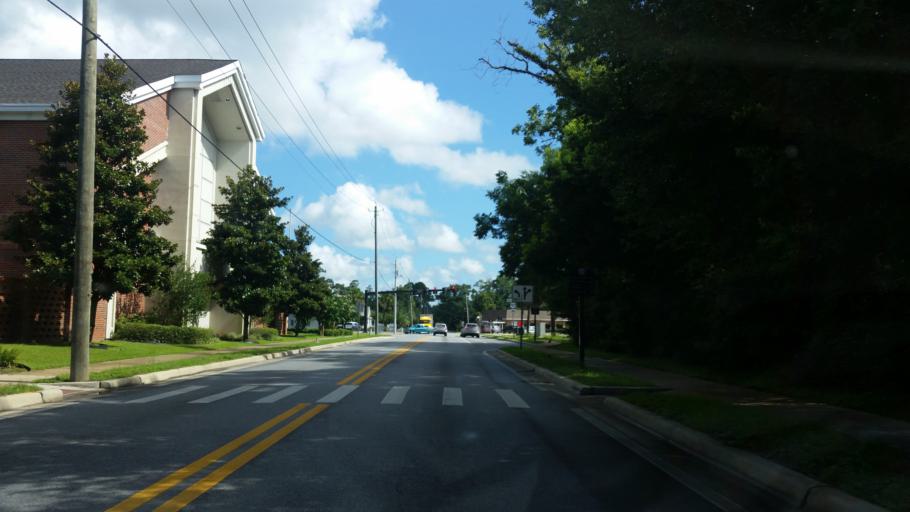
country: US
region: Florida
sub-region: Santa Rosa County
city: Milton
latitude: 30.6206
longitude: -87.0390
